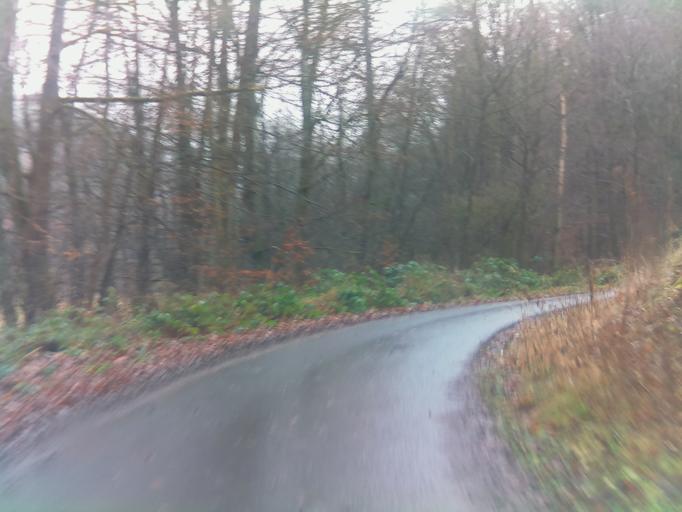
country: DE
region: Thuringia
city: Grafenroda
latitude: 50.7224
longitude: 10.7943
